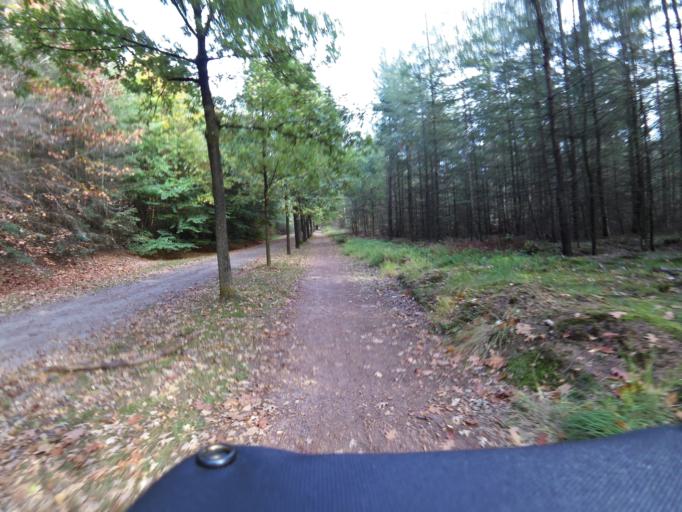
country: NL
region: North Brabant
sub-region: Gemeente Breda
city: Breda
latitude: 51.5415
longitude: 4.7571
